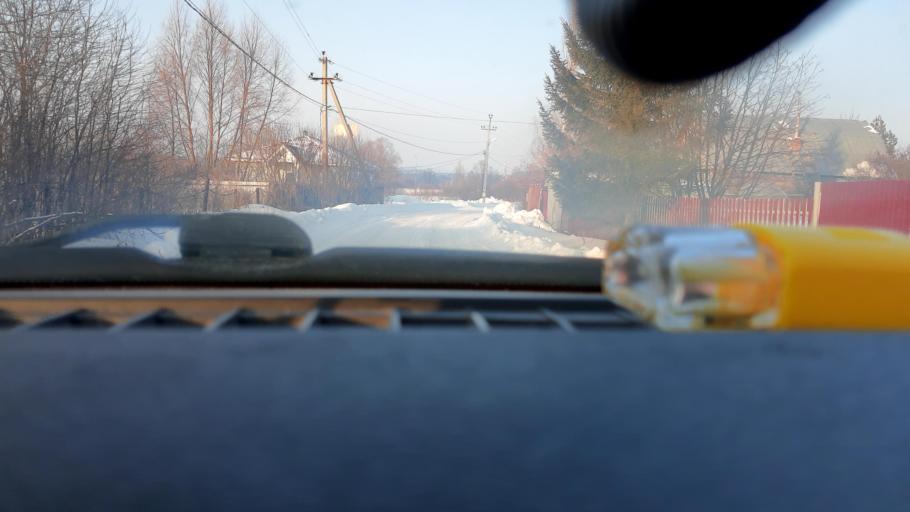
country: RU
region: Bashkortostan
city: Kabakovo
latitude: 54.6570
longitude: 56.1730
